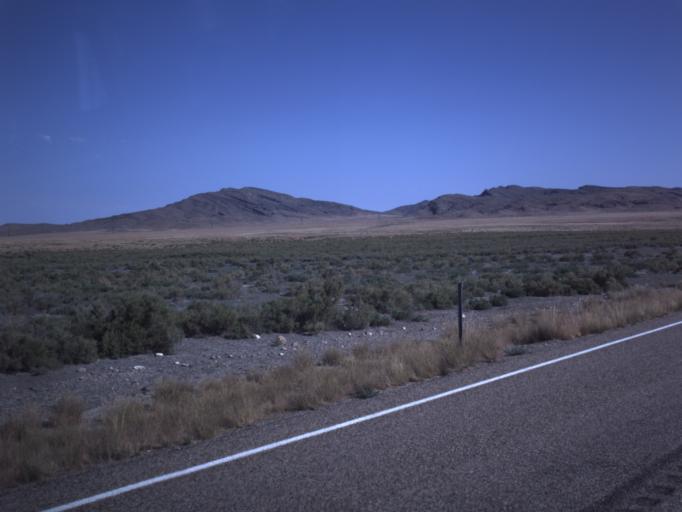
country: US
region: Utah
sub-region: Beaver County
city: Milford
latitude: 38.7255
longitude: -112.9674
